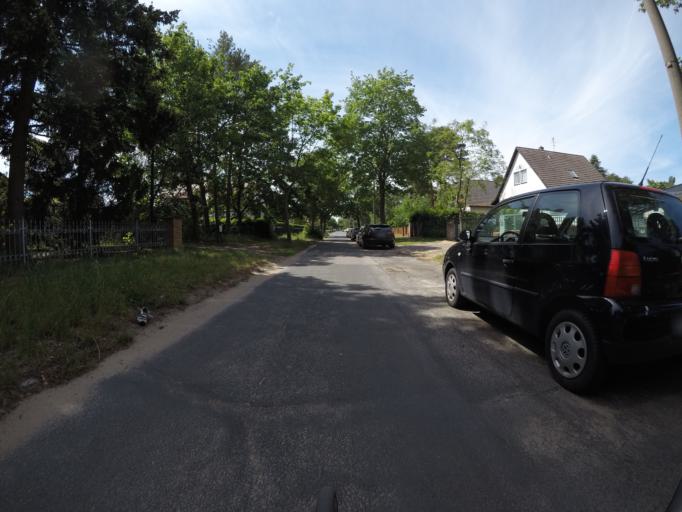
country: DE
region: Berlin
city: Mahlsdorf
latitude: 52.4870
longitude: 13.6185
